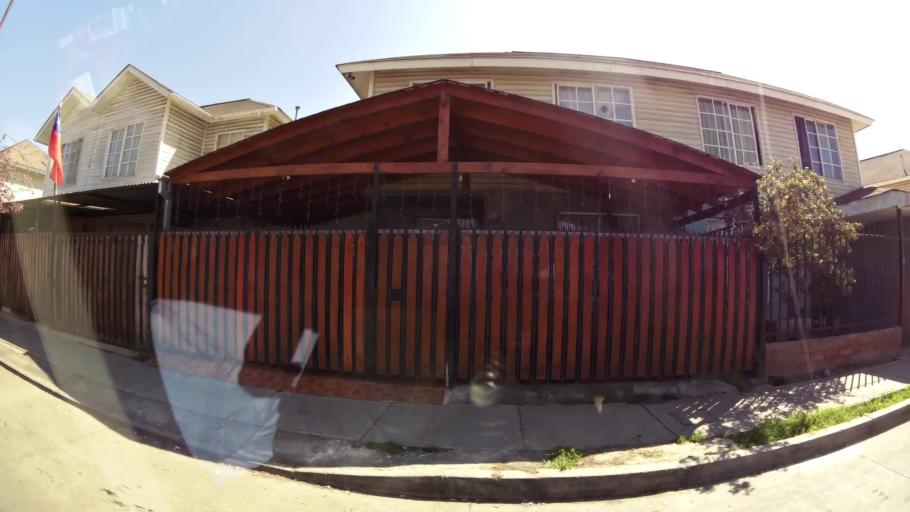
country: CL
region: Santiago Metropolitan
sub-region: Provincia de Chacabuco
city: Chicureo Abajo
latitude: -33.3298
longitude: -70.7467
